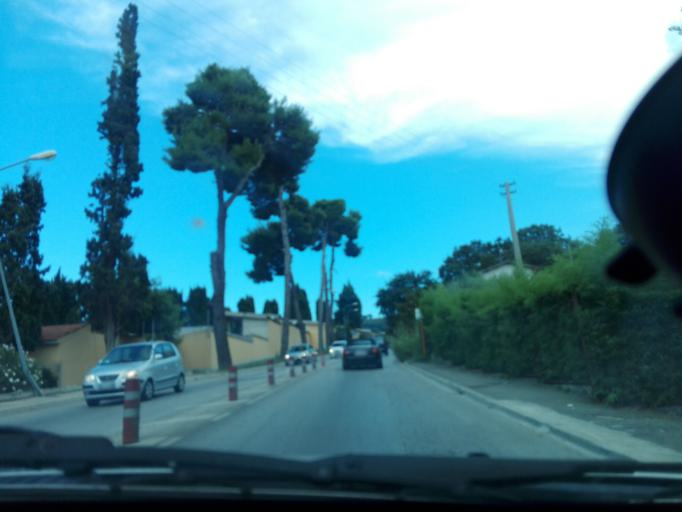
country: IT
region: Abruzzo
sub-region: Provincia di Pescara
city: Montesilvano Marina
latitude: 42.5010
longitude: 14.1386
